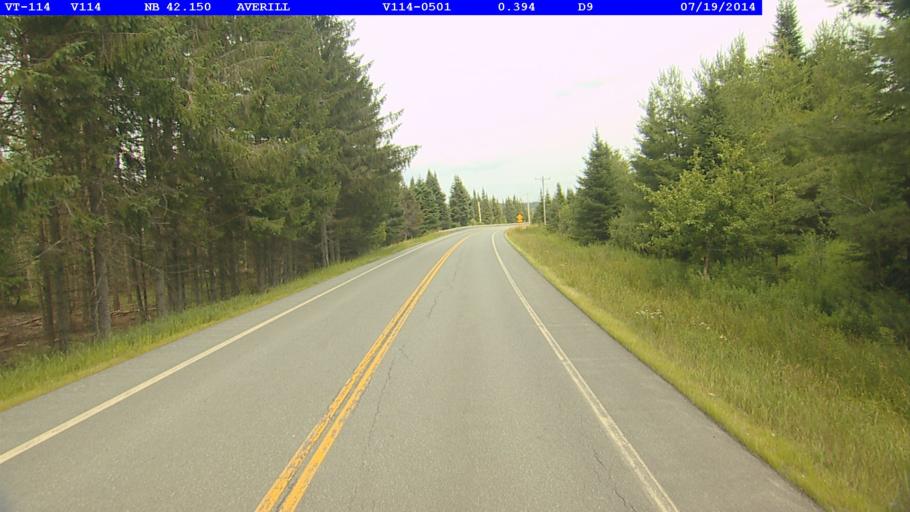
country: CA
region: Quebec
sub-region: Estrie
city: Coaticook
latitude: 45.0031
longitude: -71.7025
